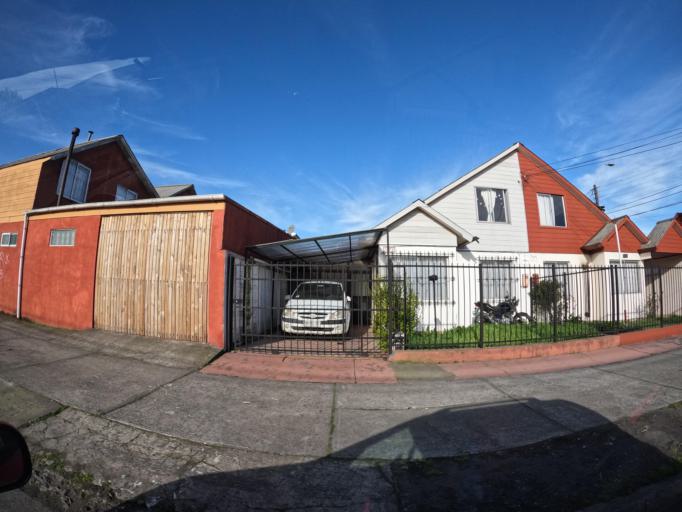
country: CL
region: Biobio
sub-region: Provincia de Concepcion
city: Talcahuano
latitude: -36.7487
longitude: -73.0866
